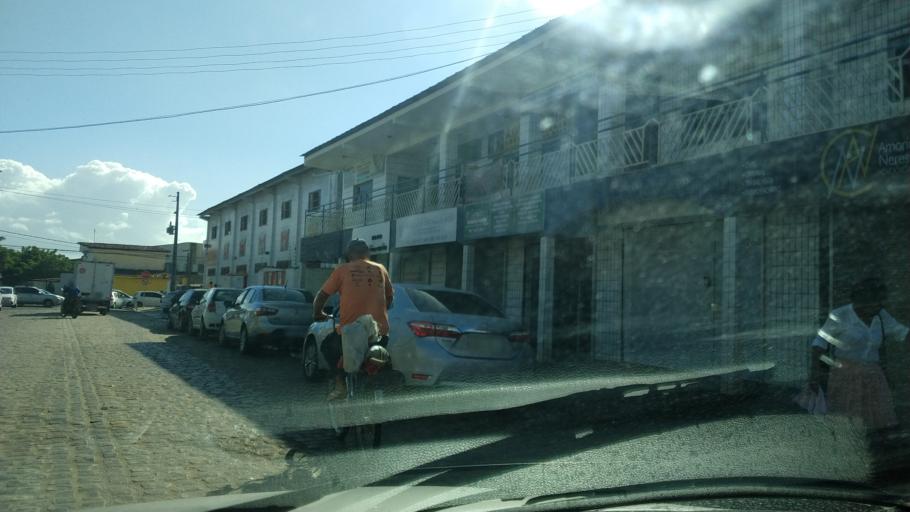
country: BR
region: Rio Grande do Norte
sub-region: Parnamirim
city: Parnamirim
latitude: -5.9156
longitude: -35.2635
